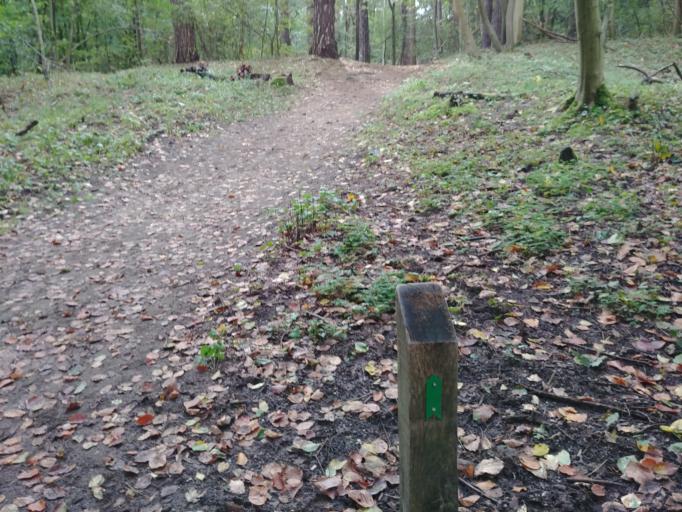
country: NL
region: North Holland
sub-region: Gemeente Heemstede
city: Heemstede
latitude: 52.3725
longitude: 4.5892
